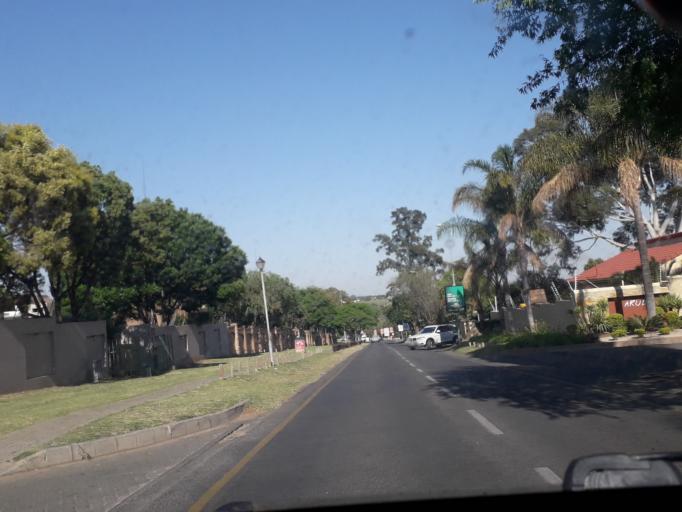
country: ZA
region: Gauteng
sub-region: City of Johannesburg Metropolitan Municipality
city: Midrand
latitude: -26.0262
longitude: 28.0694
